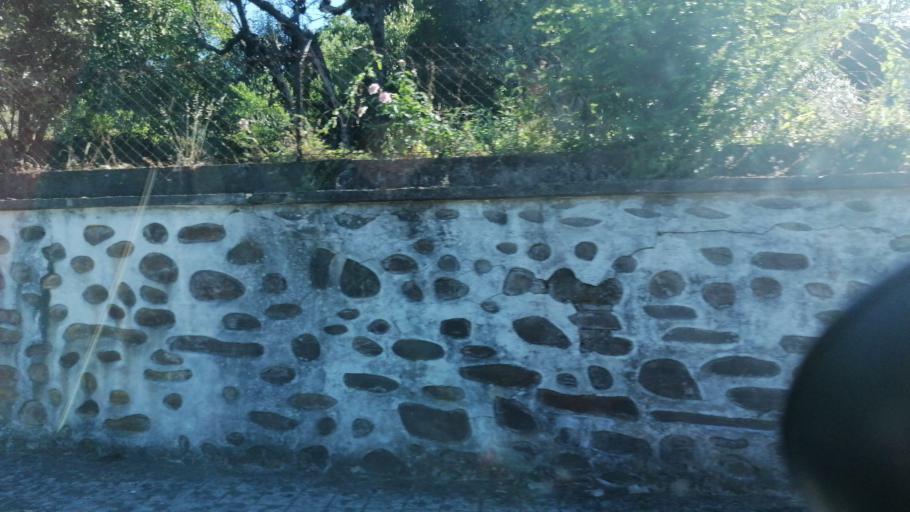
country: PT
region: Porto
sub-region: Santo Tirso
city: Santo Tirso
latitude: 41.3414
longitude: -8.4890
